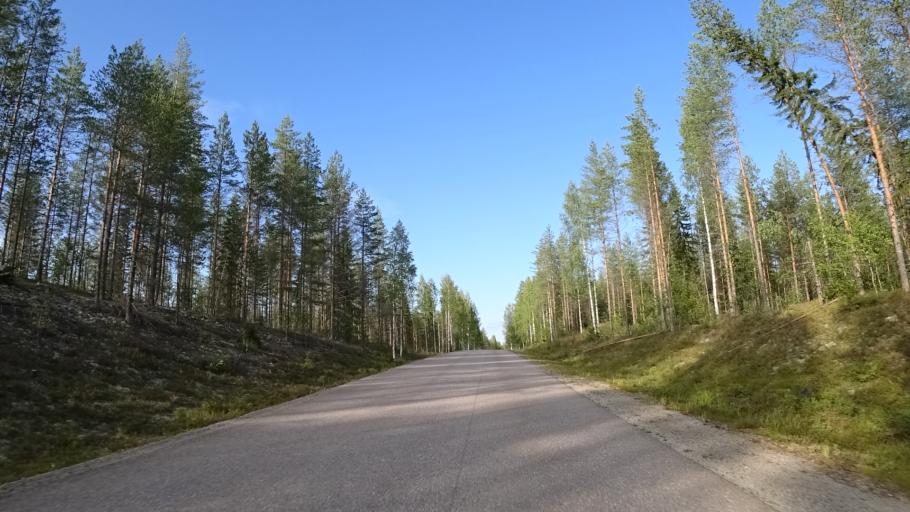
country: FI
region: North Karelia
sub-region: Joensuu
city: Eno
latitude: 63.0103
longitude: 30.4741
